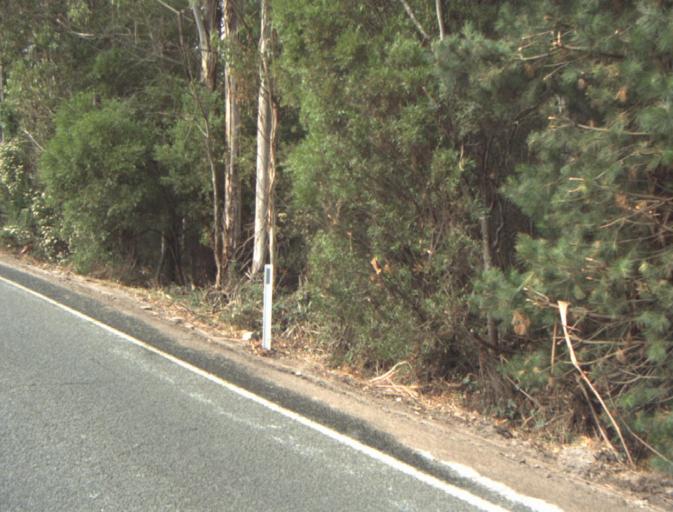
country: AU
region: Tasmania
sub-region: Launceston
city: Mayfield
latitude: -41.2740
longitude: 147.2178
